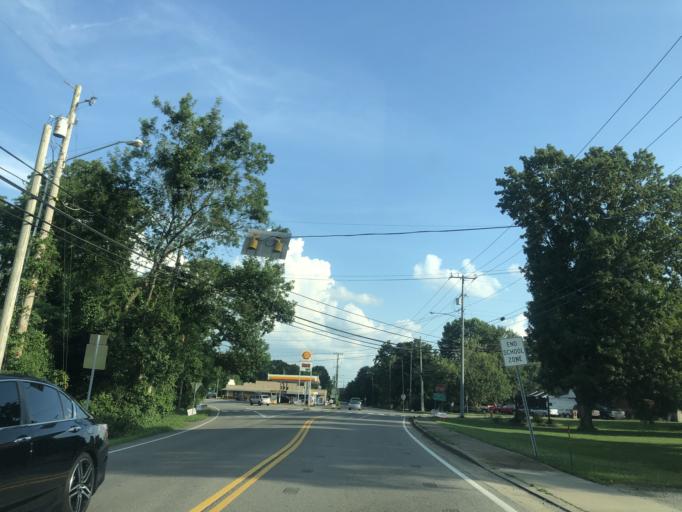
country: US
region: Tennessee
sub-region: Davidson County
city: Nashville
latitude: 36.2533
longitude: -86.8300
